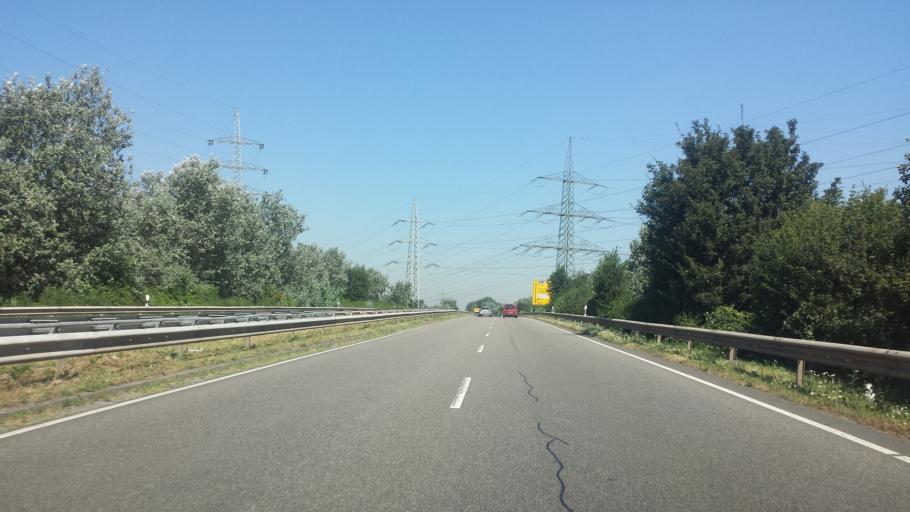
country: DE
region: Rheinland-Pfalz
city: Frankenthal
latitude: 49.5281
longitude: 8.4056
